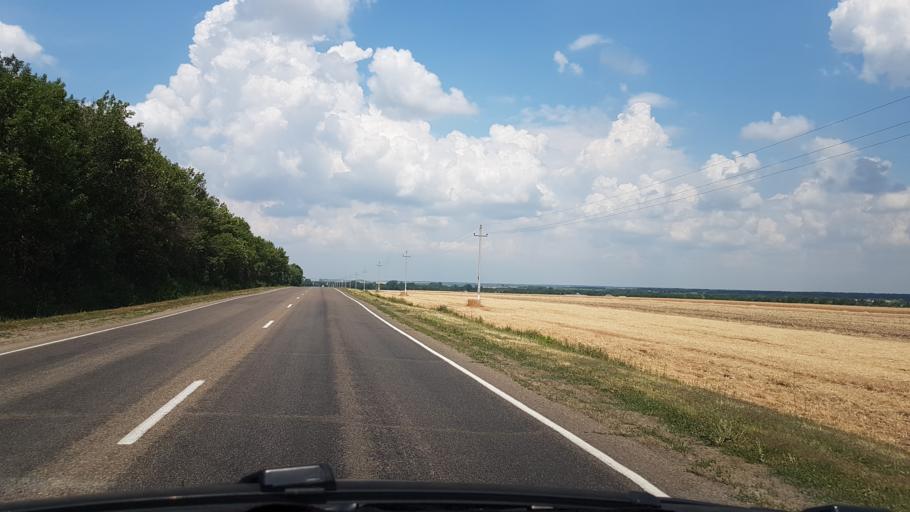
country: RU
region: Krasnodarskiy
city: Dmitriyevskaya
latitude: 45.6920
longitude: 40.7442
